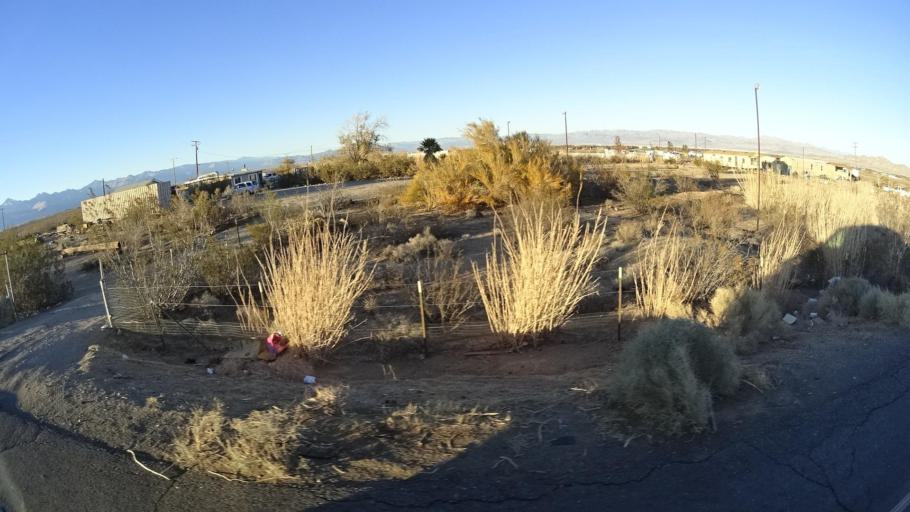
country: US
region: California
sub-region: Kern County
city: Ridgecrest
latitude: 35.6080
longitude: -117.7182
